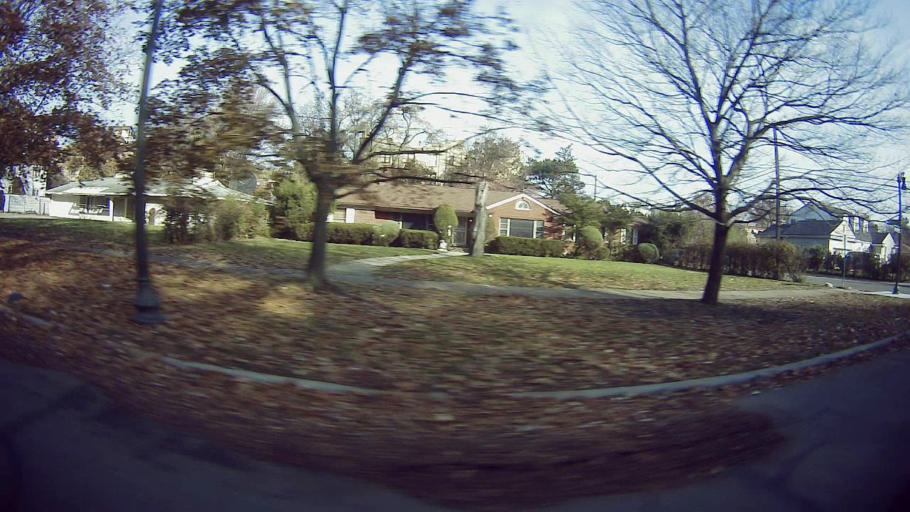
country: US
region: Michigan
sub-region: Wayne County
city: Highland Park
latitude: 42.4205
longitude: -83.1184
